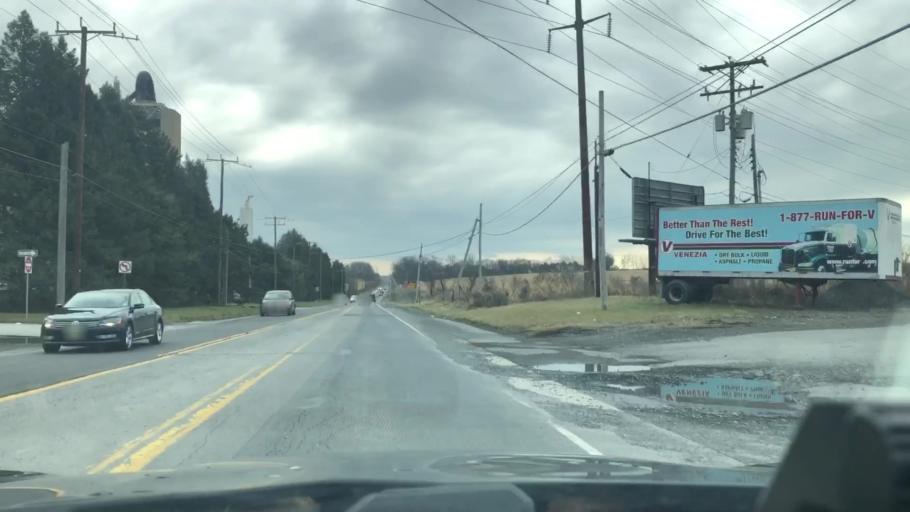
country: US
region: Pennsylvania
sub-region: Northampton County
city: Nazareth
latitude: 40.7303
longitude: -75.3047
